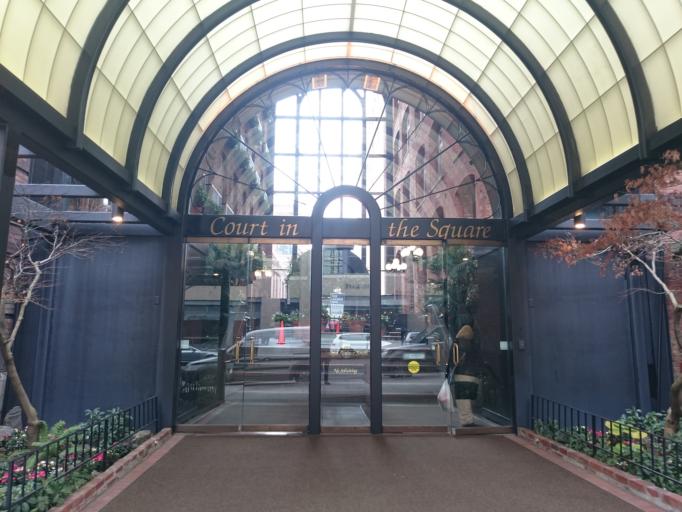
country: US
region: Washington
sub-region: King County
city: Seattle
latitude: 47.5989
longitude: -122.3318
